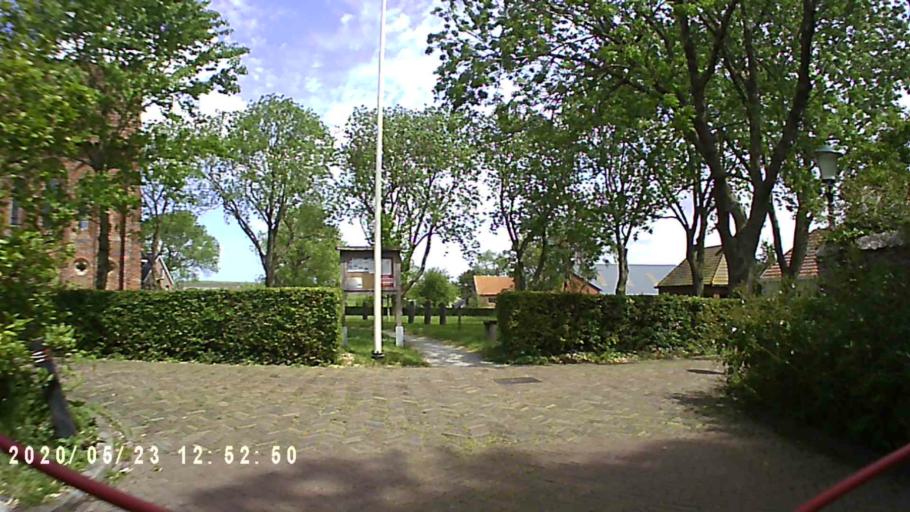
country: NL
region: Groningen
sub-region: Gemeente Delfzijl
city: Delfzijl
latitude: 53.2976
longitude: 7.0466
